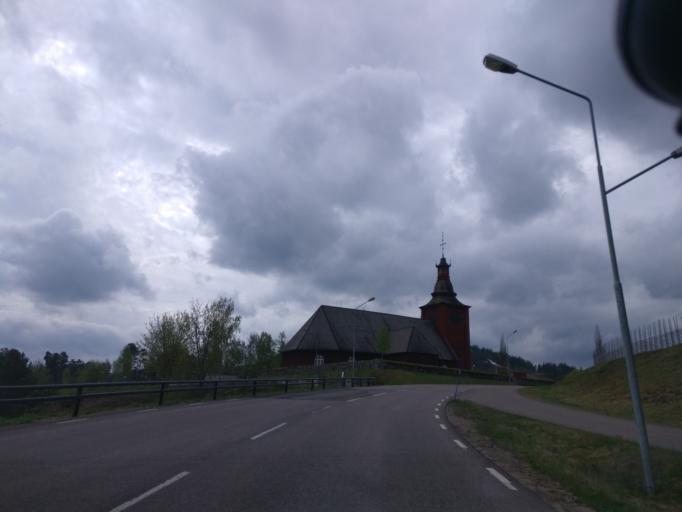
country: SE
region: Vaermland
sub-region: Hagfors Kommun
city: Ekshaerad
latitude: 60.1734
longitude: 13.4988
